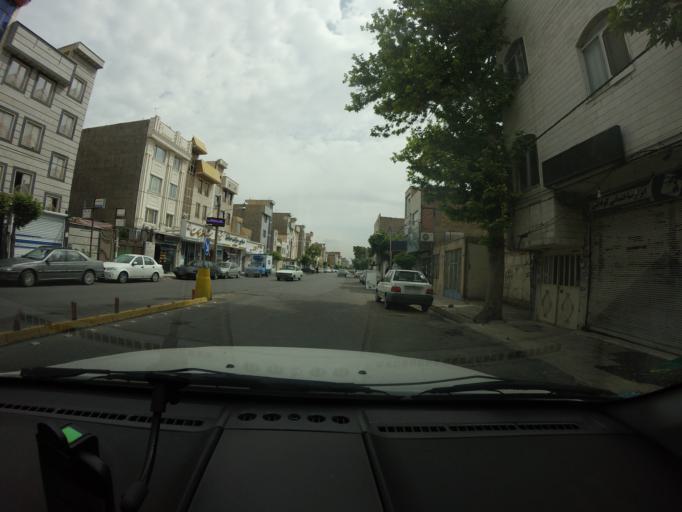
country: IR
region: Tehran
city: Eslamshahr
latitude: 35.5495
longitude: 51.2492
